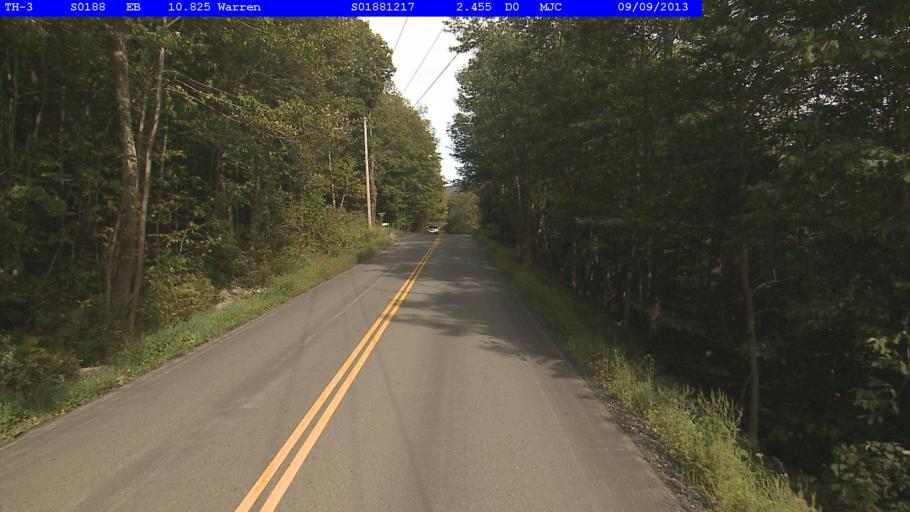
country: US
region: Vermont
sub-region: Addison County
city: Bristol
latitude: 44.1023
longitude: -72.8835
